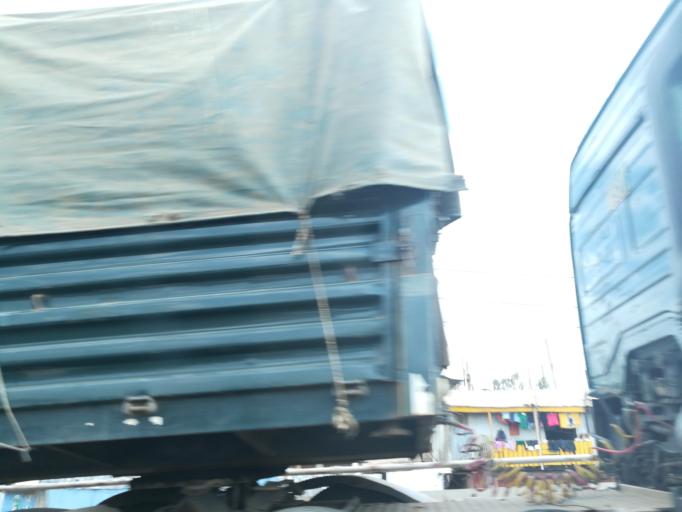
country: KE
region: Nairobi Area
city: Nairobi
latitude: -1.3184
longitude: 36.7786
